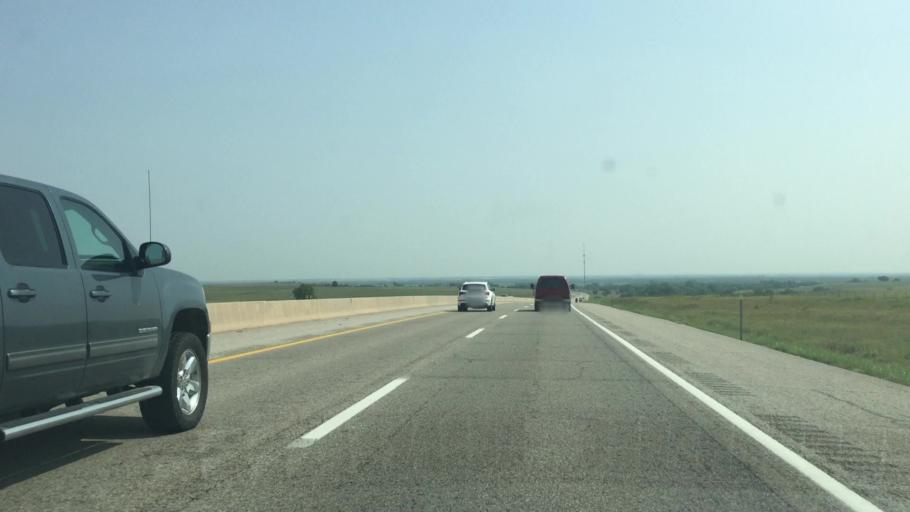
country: US
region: Kansas
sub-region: Lyon County
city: Emporia
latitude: 38.3233
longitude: -96.3192
